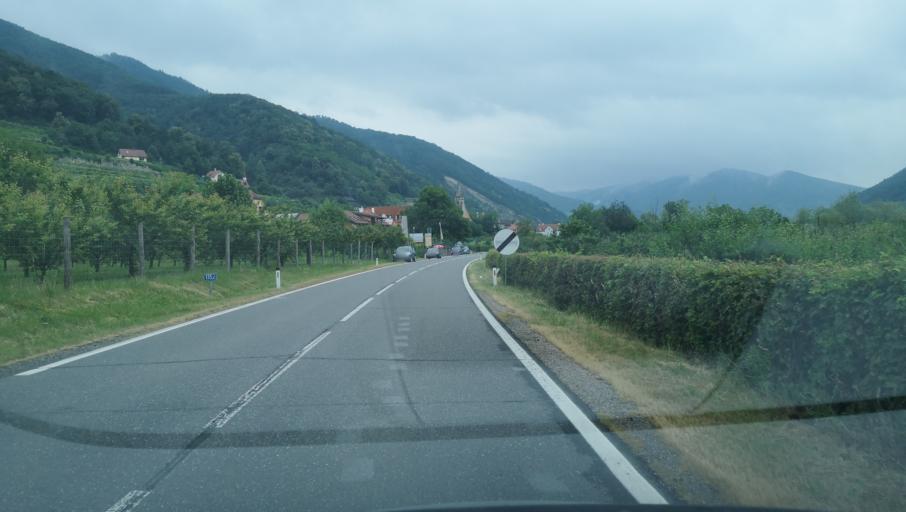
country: AT
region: Lower Austria
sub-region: Politischer Bezirk Krems
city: Spitz
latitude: 48.3361
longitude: 15.4040
